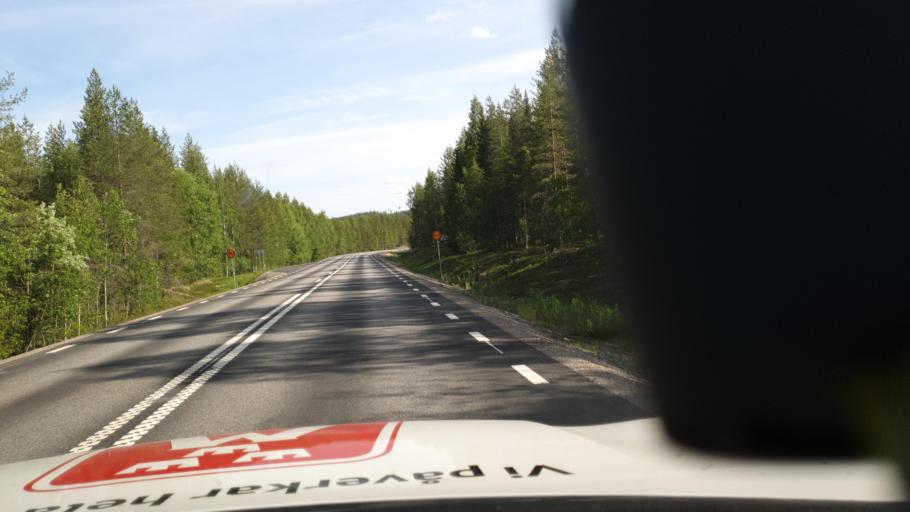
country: SE
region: Vaesterbotten
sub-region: Skelleftea Kommun
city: Boliden
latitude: 64.8825
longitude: 20.3888
